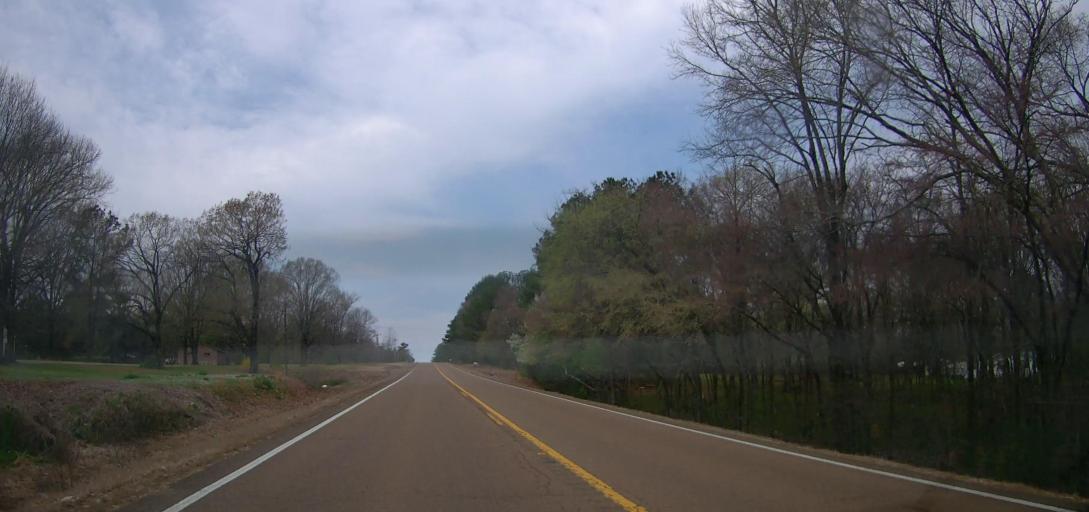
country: US
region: Mississippi
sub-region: Marshall County
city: Byhalia
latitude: 34.8379
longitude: -89.5936
